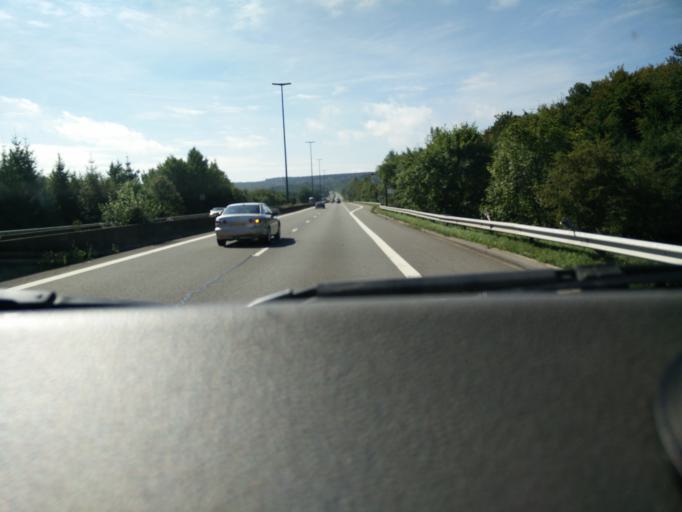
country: BE
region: Wallonia
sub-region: Province du Luxembourg
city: Tellin
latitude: 50.0404
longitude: 5.2119
